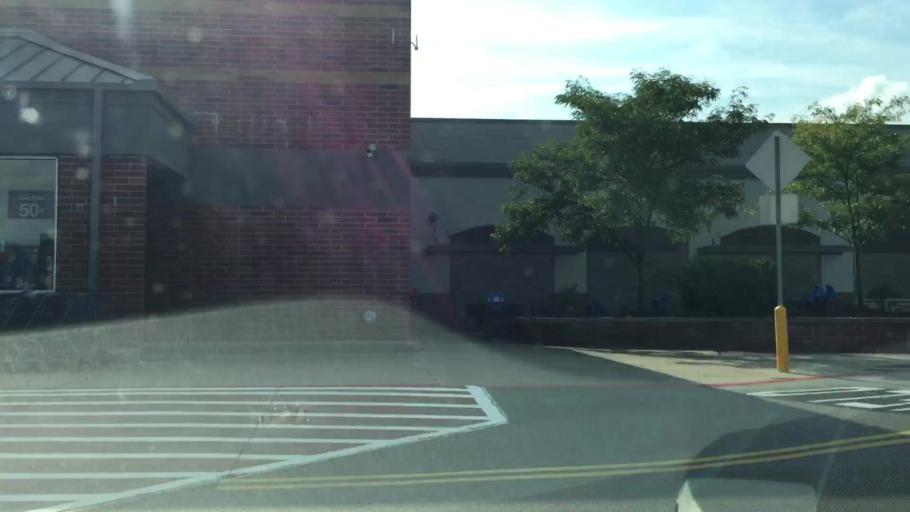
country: US
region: Pennsylvania
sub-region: Butler County
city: Cranberry Township
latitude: 40.6883
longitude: -80.1049
